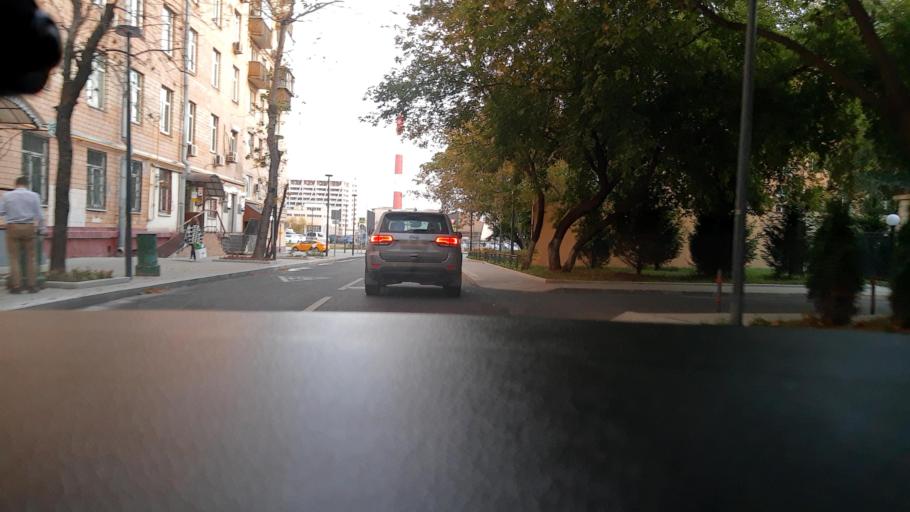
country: RU
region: Moskovskaya
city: Presnenskiy
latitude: 55.7451
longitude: 37.5525
